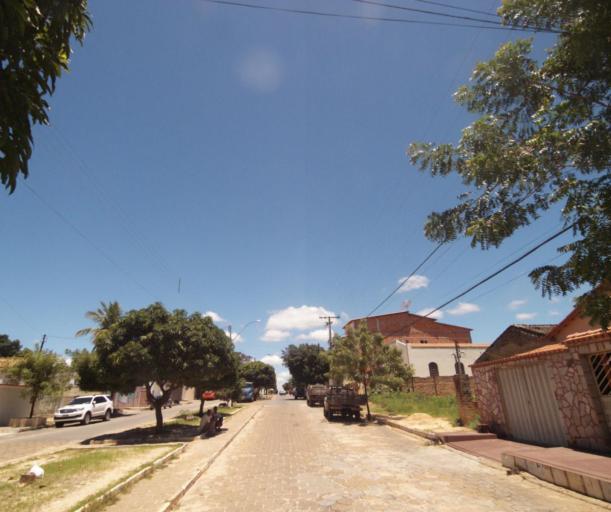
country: BR
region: Bahia
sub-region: Carinhanha
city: Carinhanha
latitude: -14.2996
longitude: -43.7705
